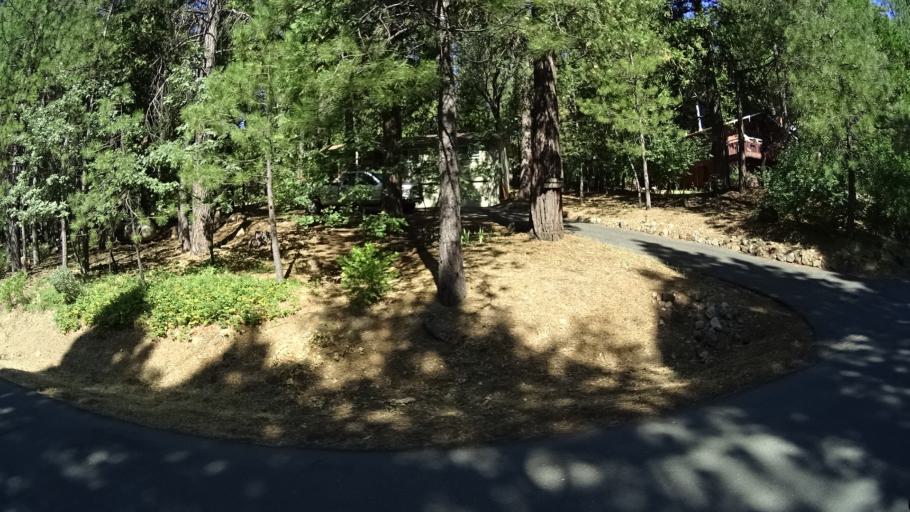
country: US
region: California
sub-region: Calaveras County
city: Arnold
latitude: 38.2536
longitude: -120.3645
